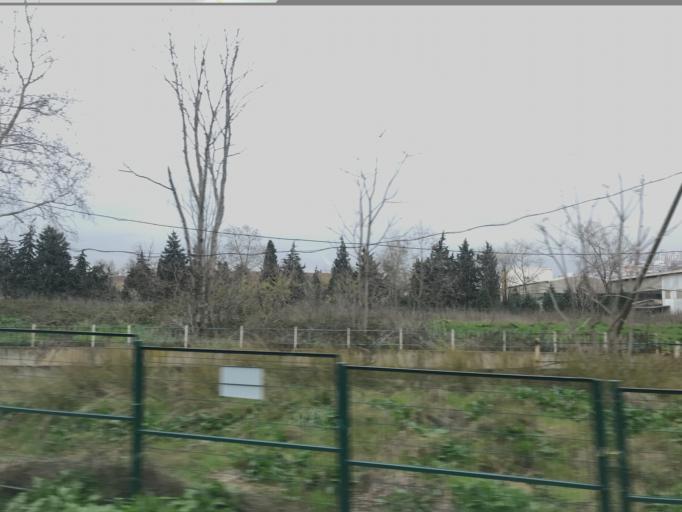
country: TR
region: Kocaeli
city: Darica
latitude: 40.8070
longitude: 29.3675
